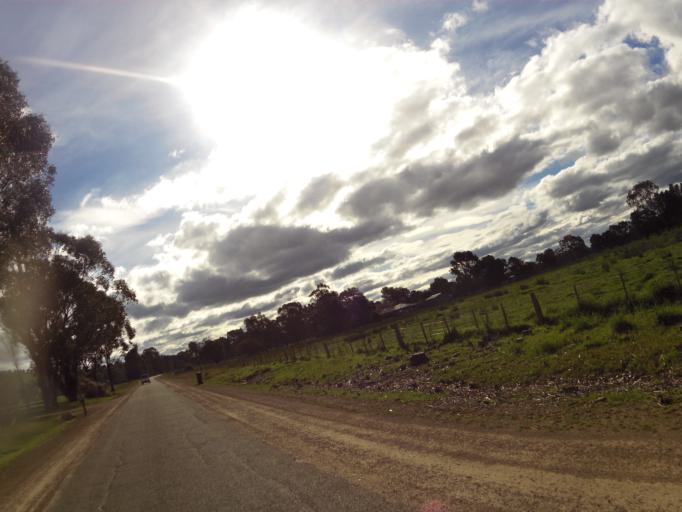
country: AU
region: Victoria
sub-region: Benalla
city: Benalla
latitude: -36.6516
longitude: 145.8887
